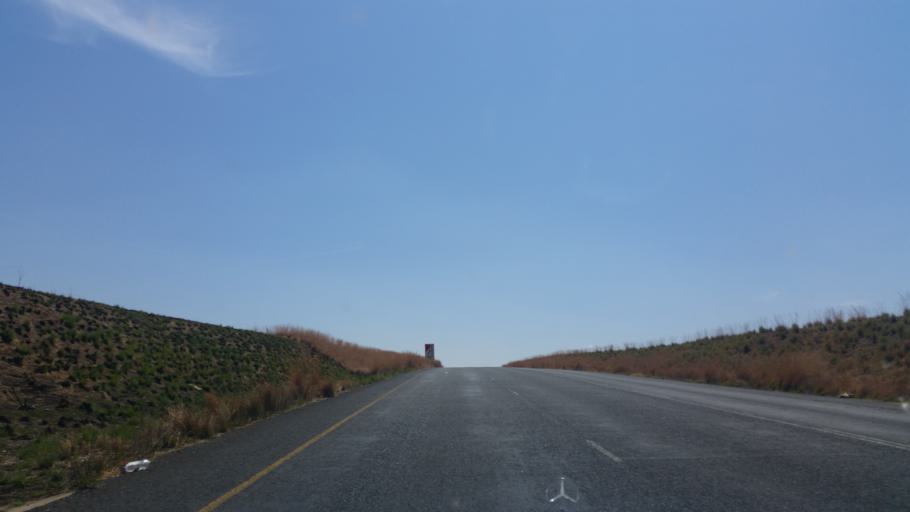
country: ZA
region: Orange Free State
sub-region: Thabo Mofutsanyana District Municipality
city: Phuthaditjhaba
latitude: -28.1713
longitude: 28.6840
